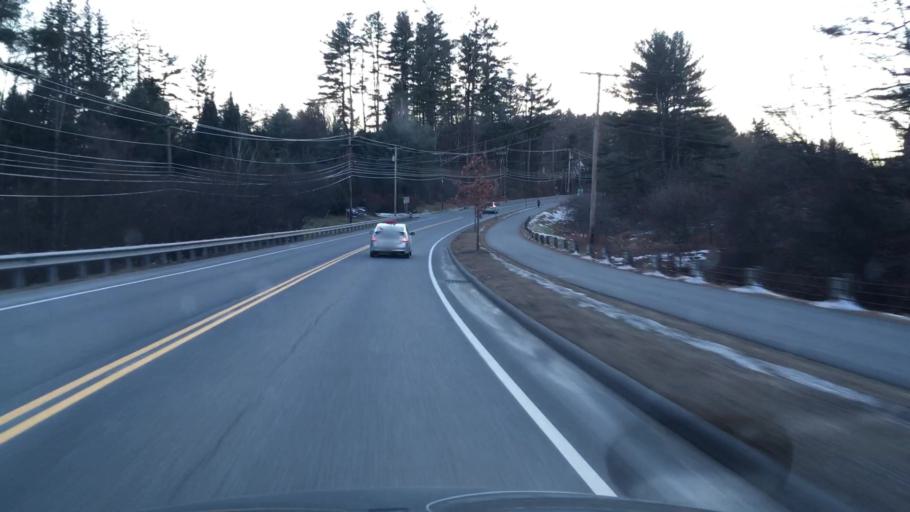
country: US
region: New Hampshire
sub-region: Grafton County
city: Hanover
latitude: 43.7097
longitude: -72.2796
